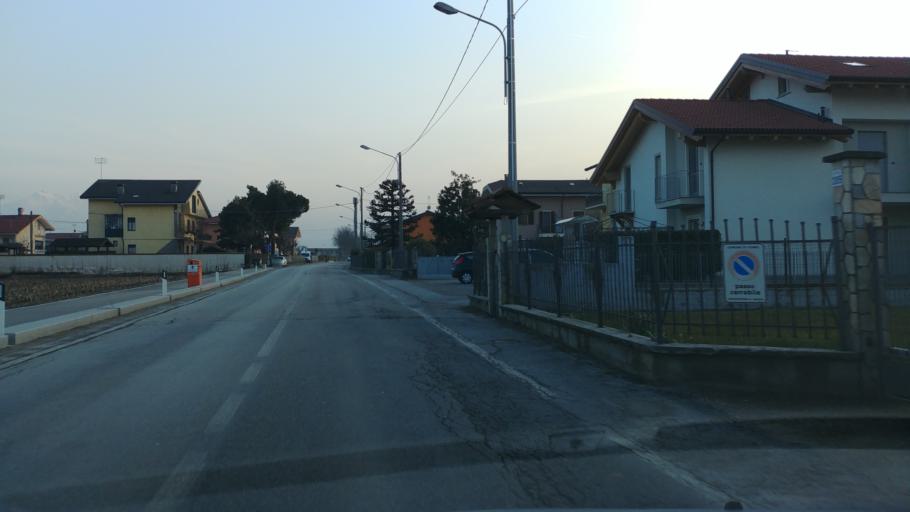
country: IT
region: Piedmont
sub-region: Provincia di Cuneo
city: Roata Rossi
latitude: 44.4296
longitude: 7.5064
